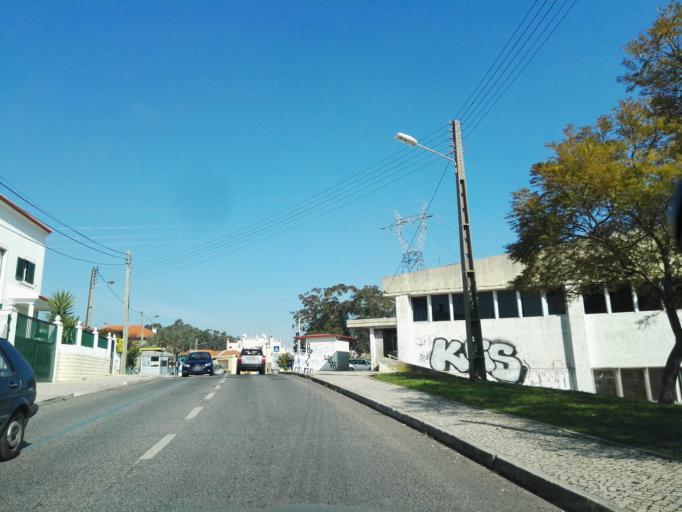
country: PT
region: Lisbon
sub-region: Odivelas
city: Povoa de Santo Adriao
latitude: 38.8009
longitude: -9.1651
